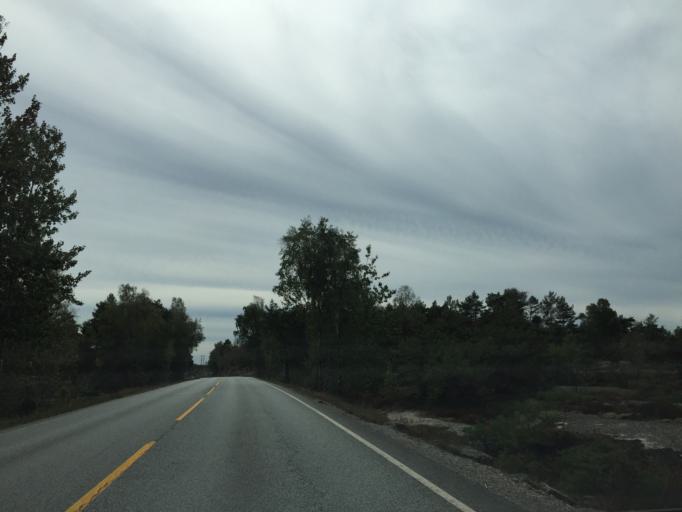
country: NO
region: Ostfold
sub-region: Hvaler
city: Skjaerhalden
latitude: 59.0901
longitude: 10.9265
